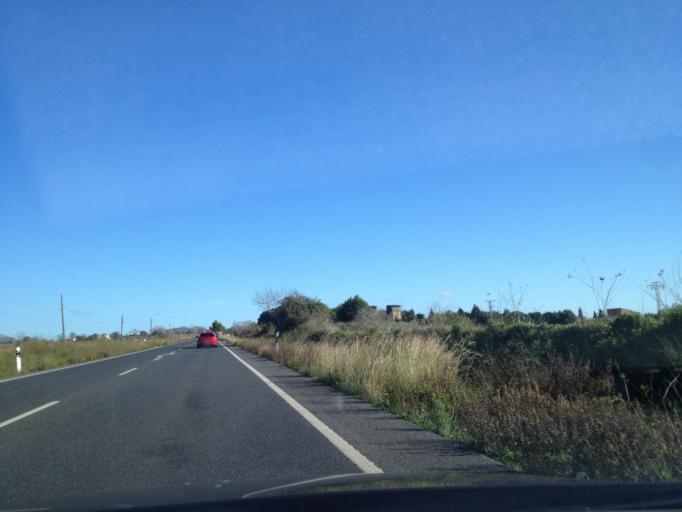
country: ES
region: Balearic Islands
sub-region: Illes Balears
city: Sant Llorenc des Cardassar
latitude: 39.5926
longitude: 3.2588
